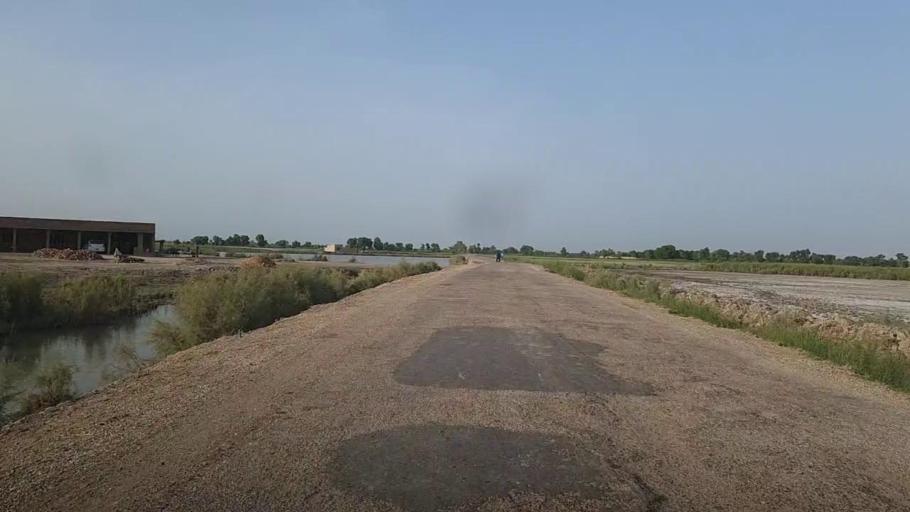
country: PK
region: Sindh
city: Ubauro
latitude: 28.0947
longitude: 69.8069
